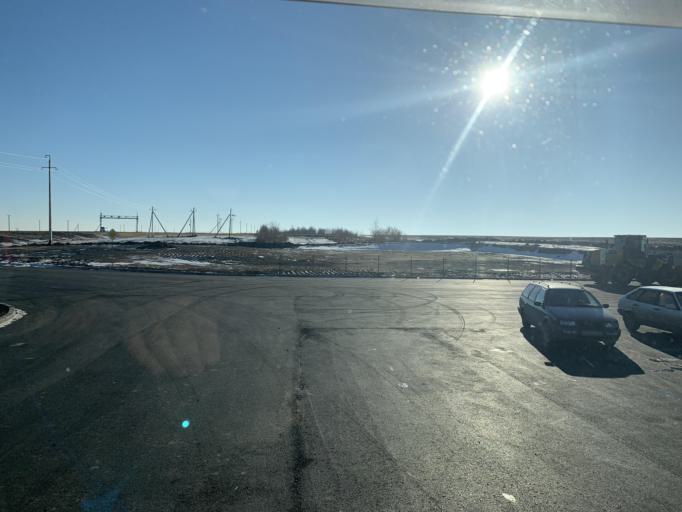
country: KZ
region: Batys Qazaqstan
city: Peremetnoe
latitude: 51.6554
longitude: 51.0084
